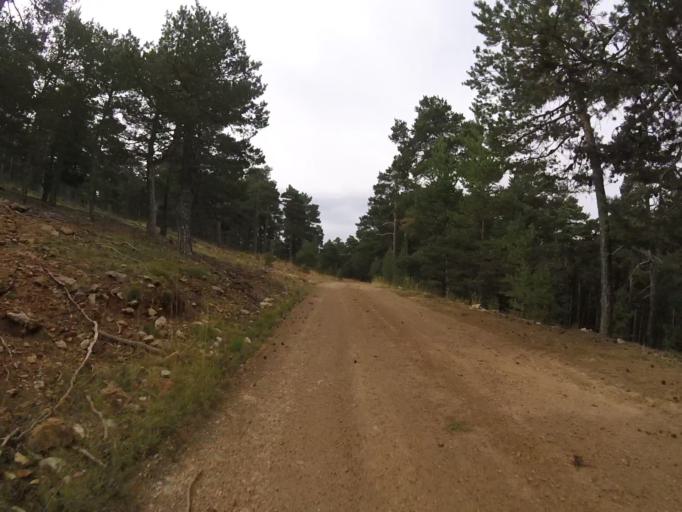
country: ES
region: Aragon
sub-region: Provincia de Teruel
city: Valdelinares
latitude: 40.3545
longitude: -0.5983
